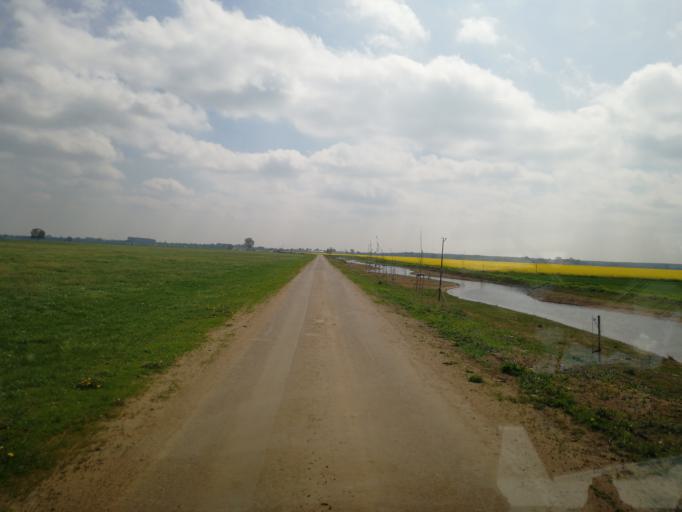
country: DE
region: Brandenburg
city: Doberlug-Kirchhain
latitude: 51.6741
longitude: 13.5368
